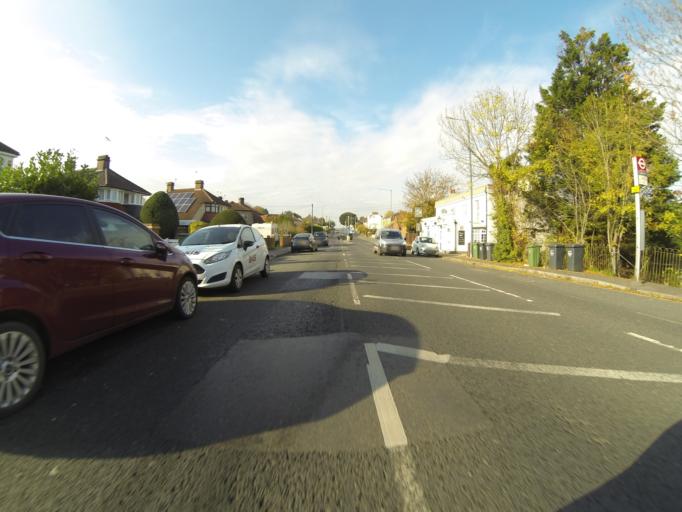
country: GB
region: England
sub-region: Kent
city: Dartford
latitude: 51.4481
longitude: 0.1945
